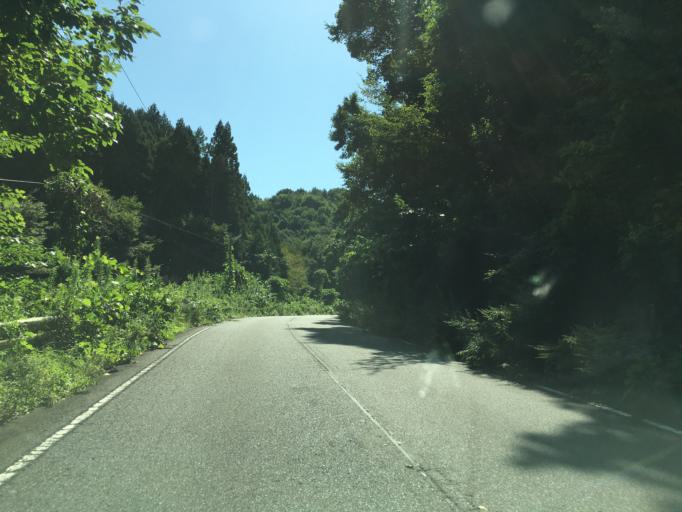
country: JP
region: Fukushima
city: Sukagawa
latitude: 37.2915
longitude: 140.4873
